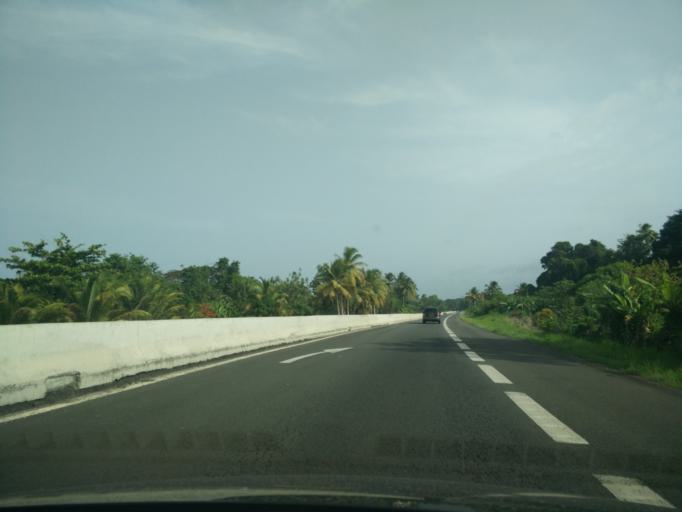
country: GP
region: Guadeloupe
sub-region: Guadeloupe
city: Petit-Bourg
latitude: 16.1682
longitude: -61.5863
